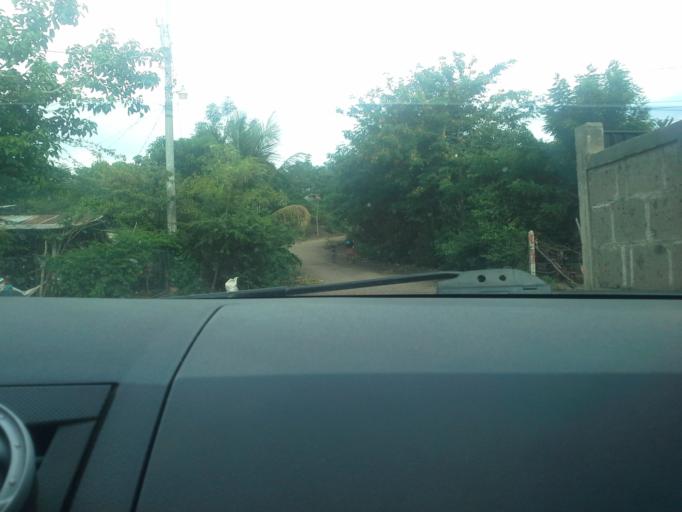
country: NI
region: Matagalpa
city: Ciudad Dario
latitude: 12.8546
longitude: -86.0897
